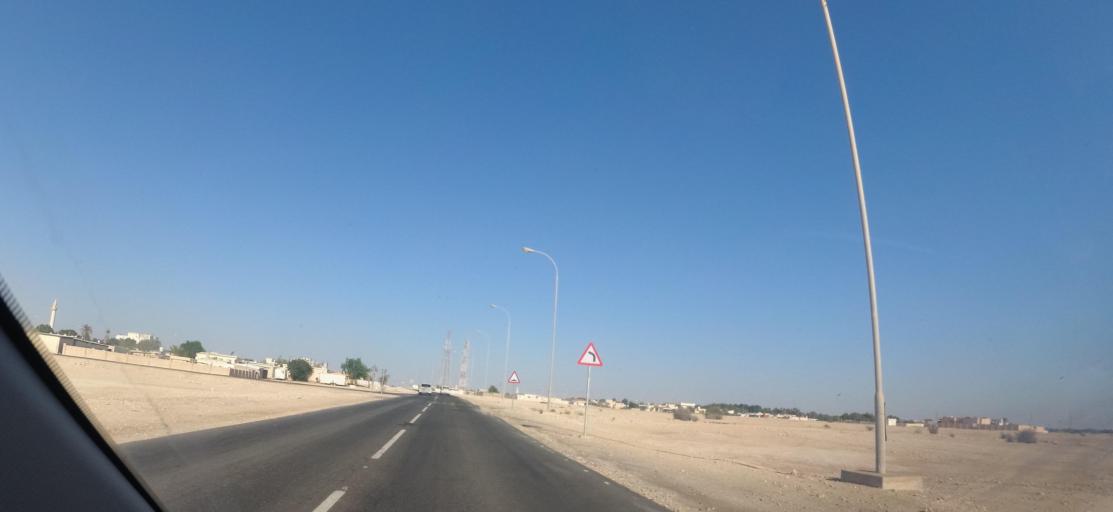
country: QA
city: Al Ghuwayriyah
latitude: 25.8254
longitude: 51.2447
